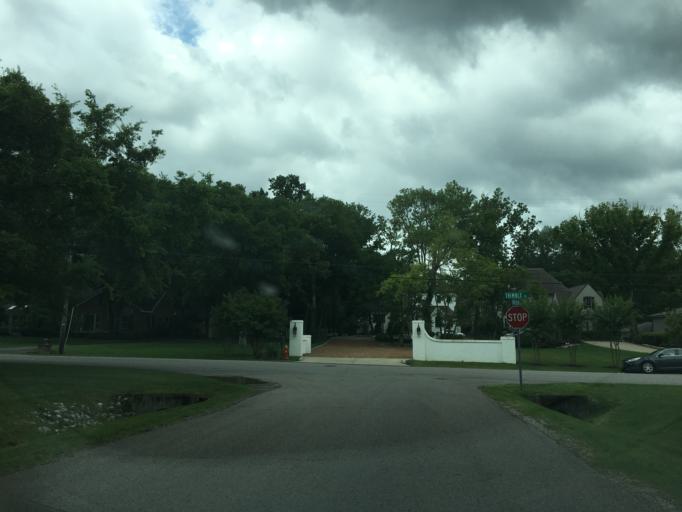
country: US
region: Tennessee
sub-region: Davidson County
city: Belle Meade
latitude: 36.0953
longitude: -86.8436
